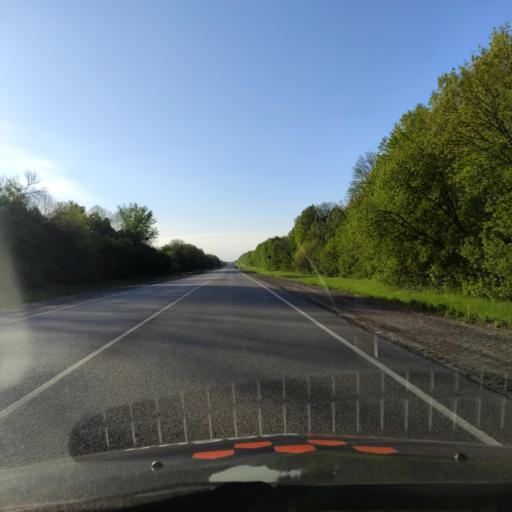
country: RU
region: Lipetsk
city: Yelets
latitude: 52.5733
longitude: 38.6540
